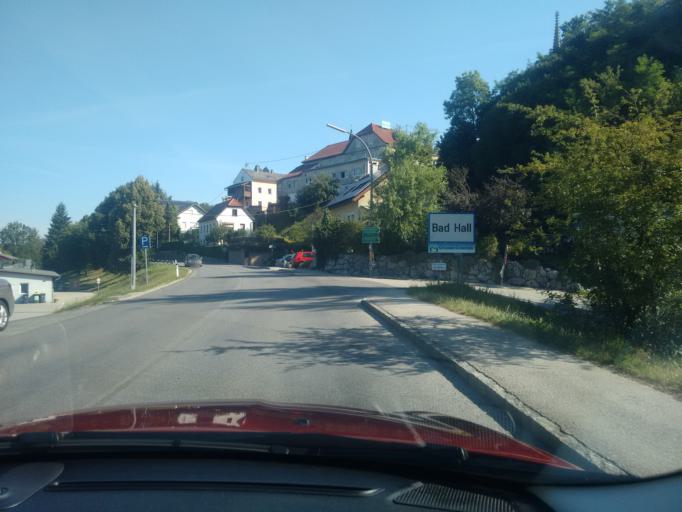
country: AT
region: Upper Austria
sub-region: Politischer Bezirk Steyr-Land
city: Bad Hall
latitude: 48.0345
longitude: 14.2034
